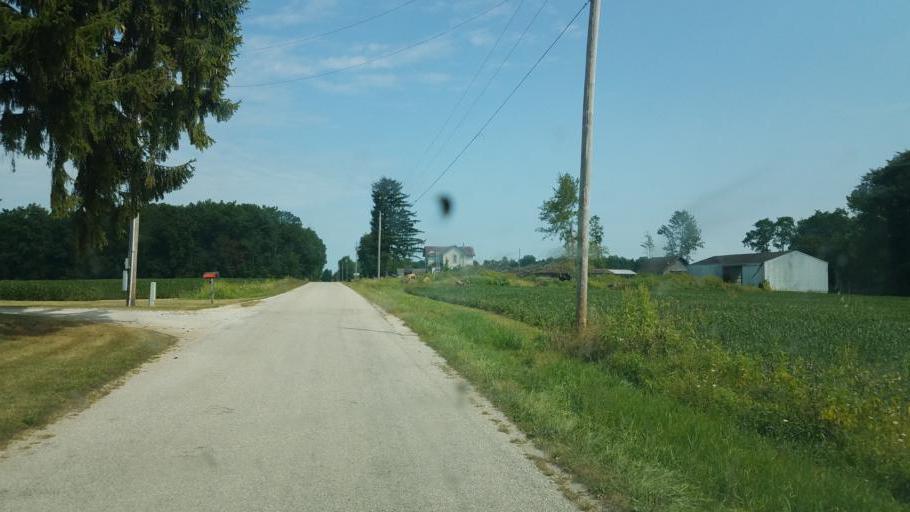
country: US
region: Ohio
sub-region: Delaware County
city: Ashley
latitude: 40.4663
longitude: -83.0475
